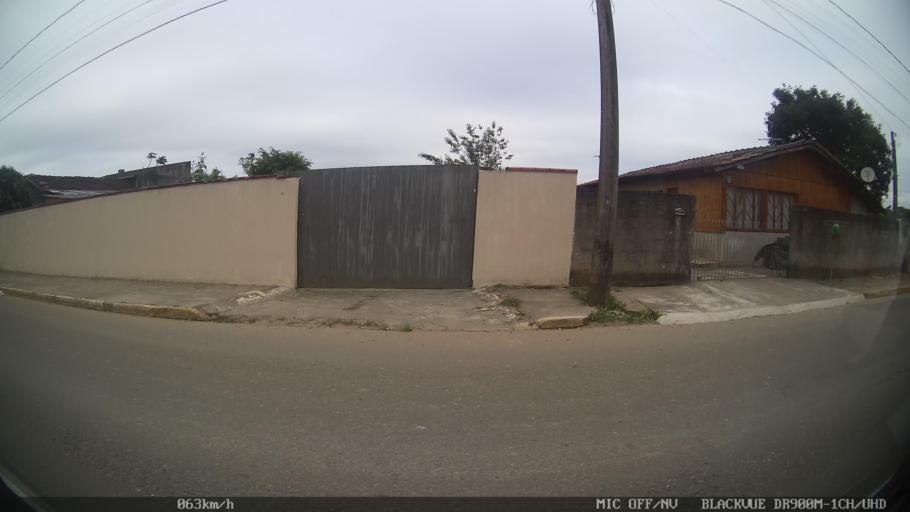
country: BR
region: Santa Catarina
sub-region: Joinville
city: Joinville
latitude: -26.3354
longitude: -48.9096
